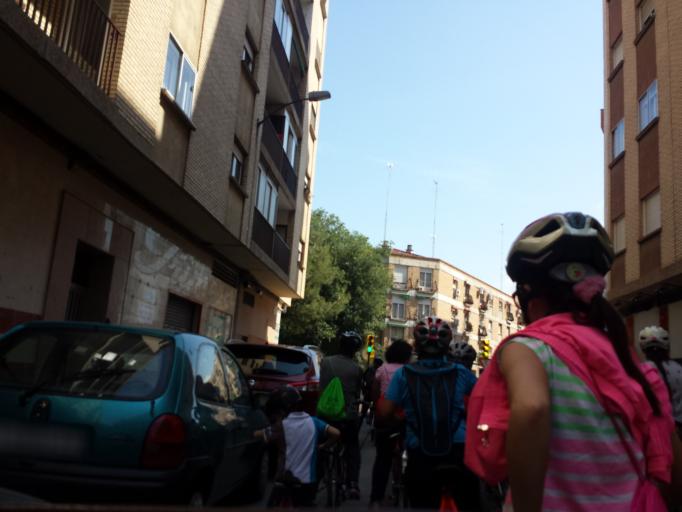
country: ES
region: Aragon
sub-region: Provincia de Zaragoza
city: Almozara
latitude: 41.6621
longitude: -0.8976
